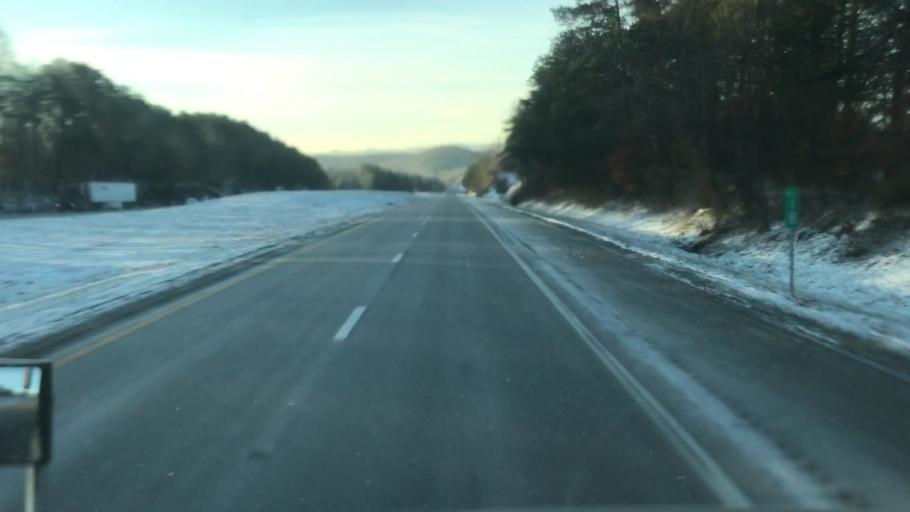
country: US
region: Kentucky
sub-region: Whitley County
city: Williamsburg
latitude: 36.8297
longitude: -84.1645
